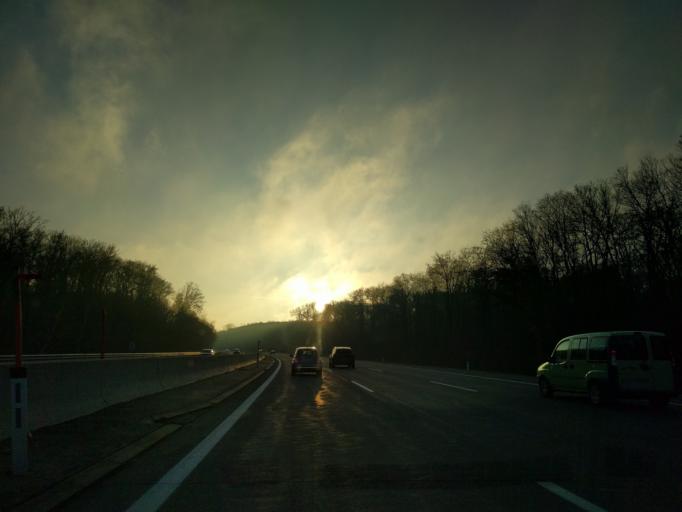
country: AT
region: Lower Austria
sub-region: Politischer Bezirk Wien-Umgebung
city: Purkersdorf
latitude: 48.2013
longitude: 16.2124
